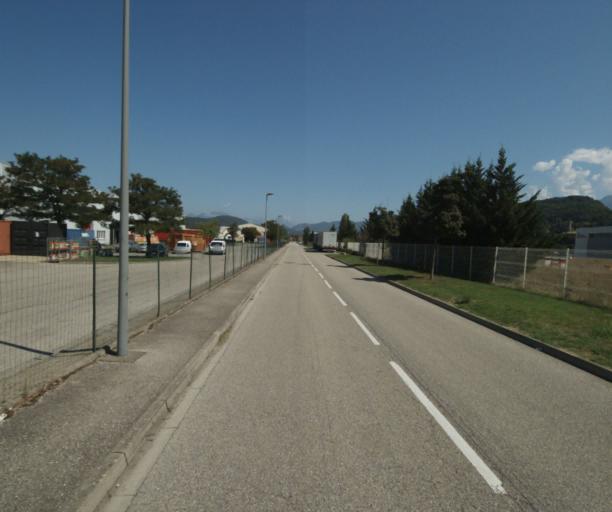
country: FR
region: Rhone-Alpes
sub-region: Departement de l'Isere
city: Champ-sur-Drac
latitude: 45.0668
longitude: 5.7226
